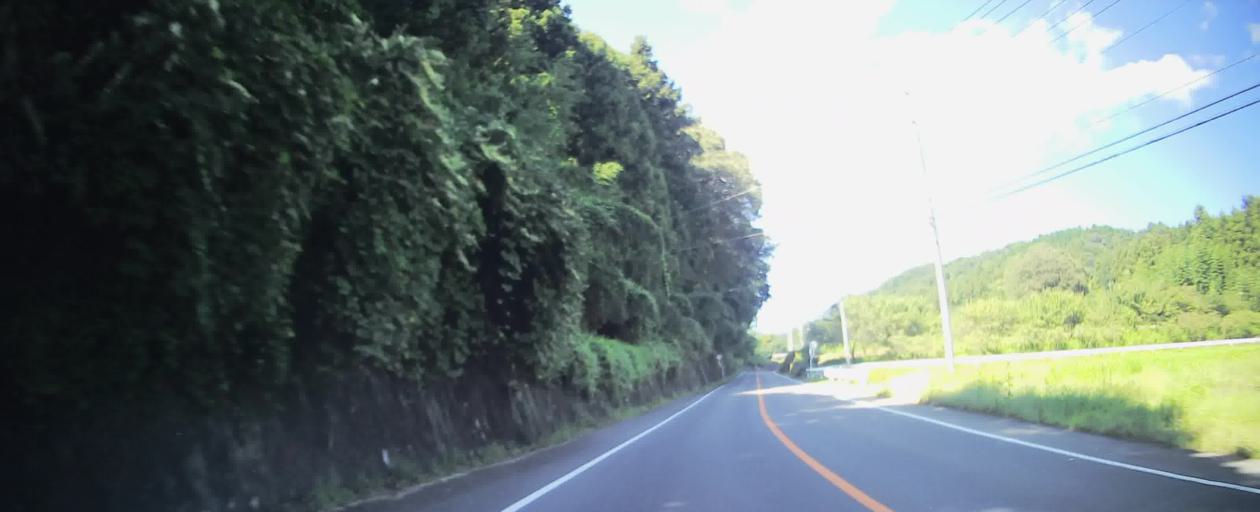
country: JP
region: Gunma
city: Kanekomachi
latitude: 36.4210
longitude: 138.9362
